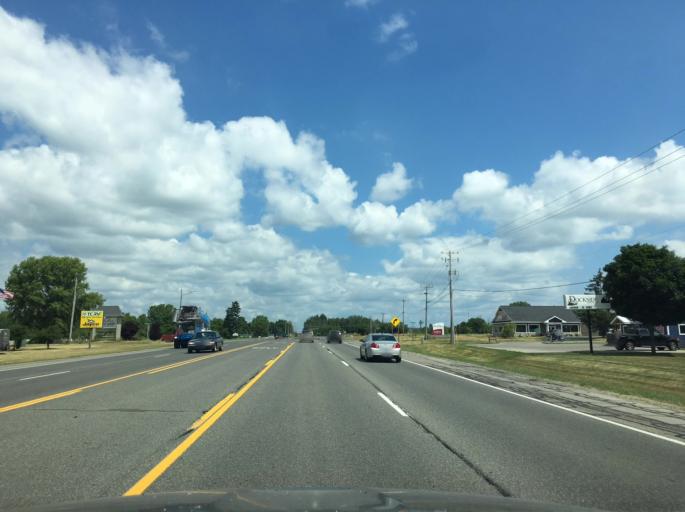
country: US
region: Michigan
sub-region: Grand Traverse County
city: Traverse City
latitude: 44.6965
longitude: -85.6562
